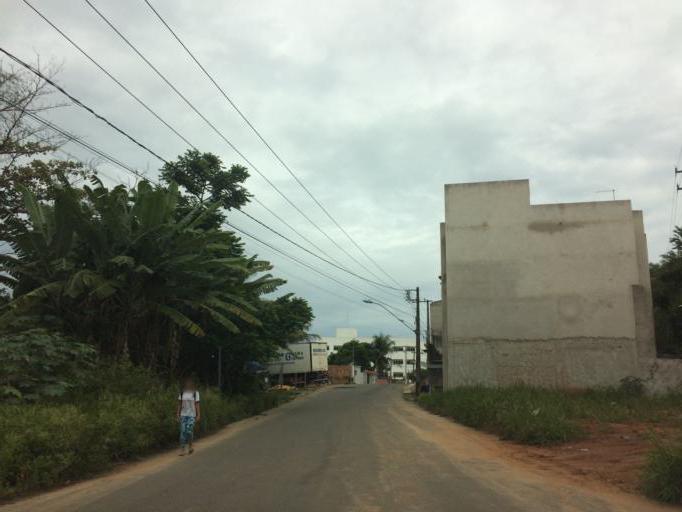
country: BR
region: Espirito Santo
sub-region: Guarapari
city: Guarapari
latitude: -20.6563
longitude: -40.5066
